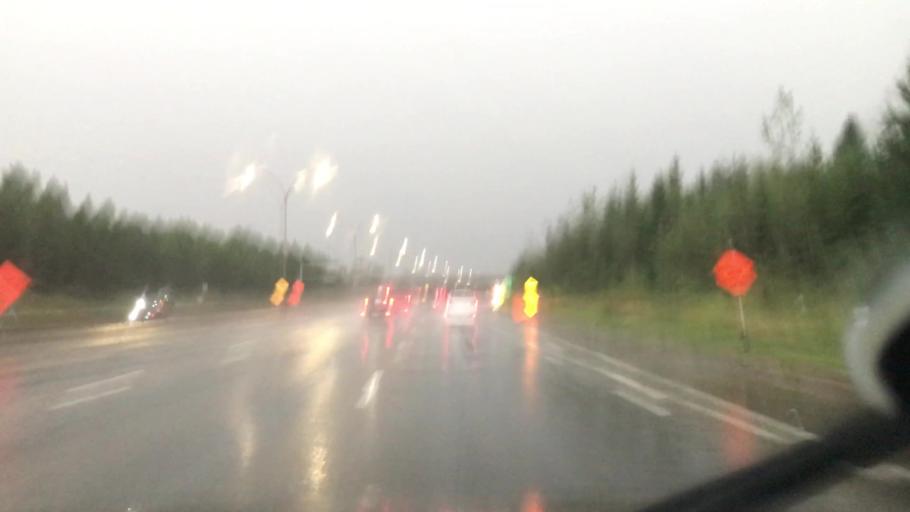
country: CA
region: Alberta
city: Edmonton
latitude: 53.4843
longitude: -113.4578
